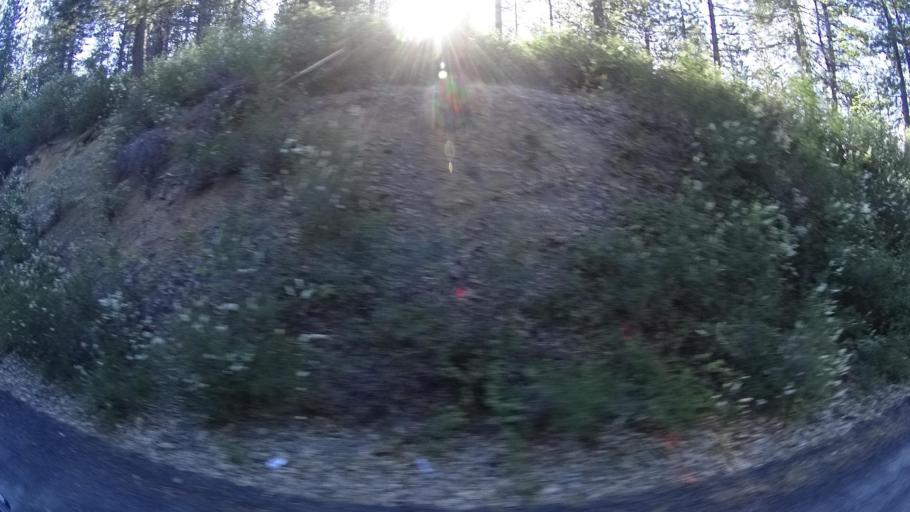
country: US
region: California
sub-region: Lake County
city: Upper Lake
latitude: 39.2870
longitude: -122.9271
